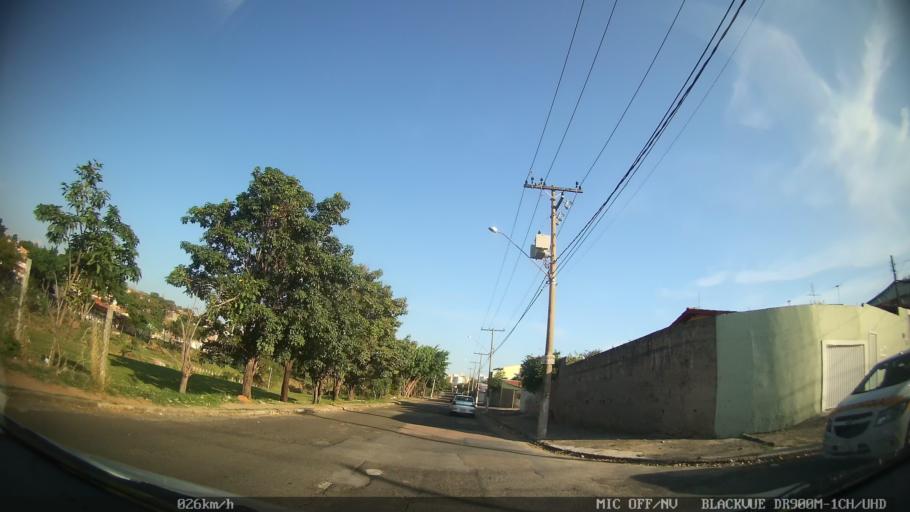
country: BR
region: Sao Paulo
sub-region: Campinas
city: Campinas
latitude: -22.9748
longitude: -47.1257
